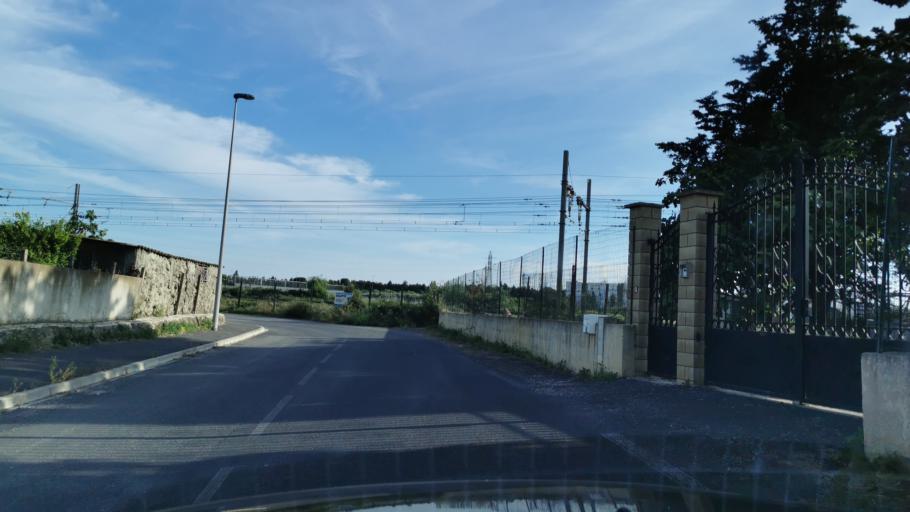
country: FR
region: Languedoc-Roussillon
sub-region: Departement de l'Aude
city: Narbonne
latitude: 43.1680
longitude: 2.9957
